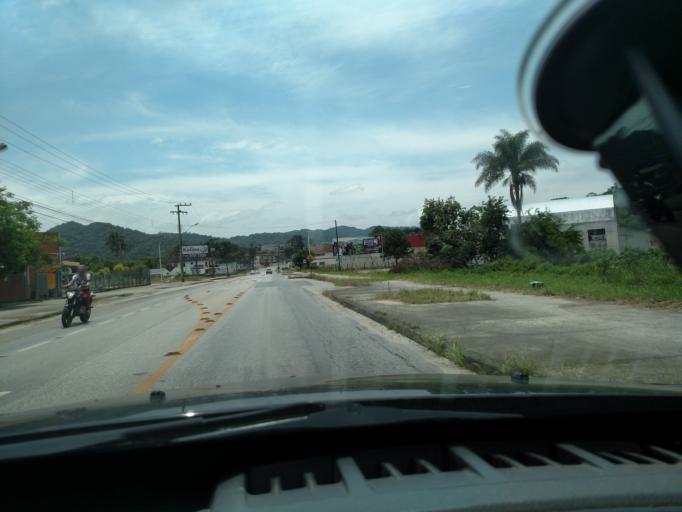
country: BR
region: Santa Catarina
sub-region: Gaspar
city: Gaspar
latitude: -26.8967
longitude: -49.0044
